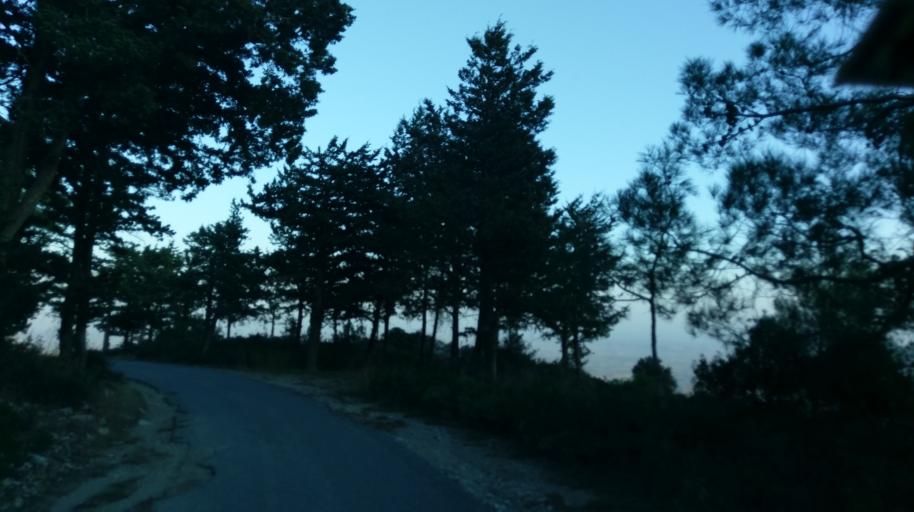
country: CY
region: Ammochostos
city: Trikomo
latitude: 35.3986
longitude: 33.9106
